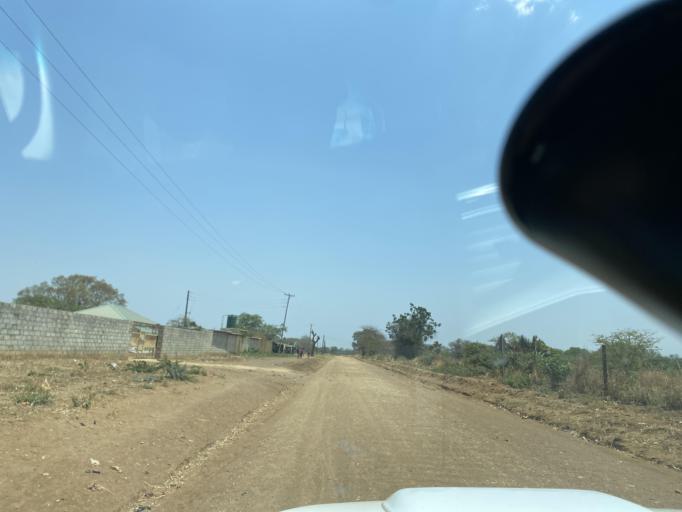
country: ZM
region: Lusaka
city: Lusaka
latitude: -15.4292
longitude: 28.0872
